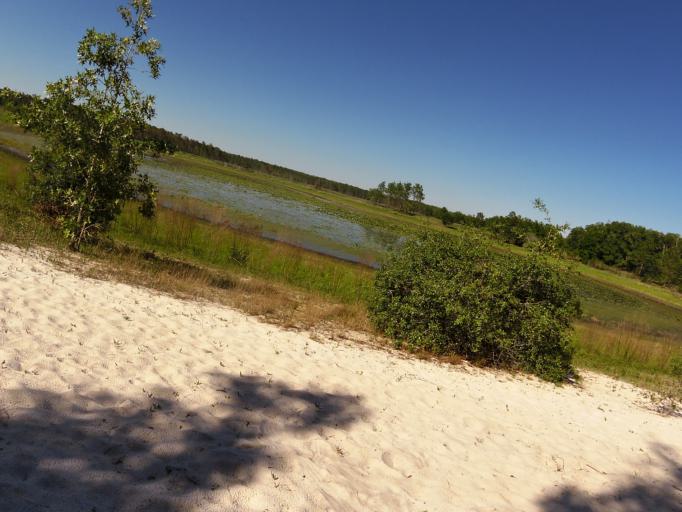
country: US
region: Florida
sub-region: Clay County
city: Keystone Heights
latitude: 29.8205
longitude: -81.9441
